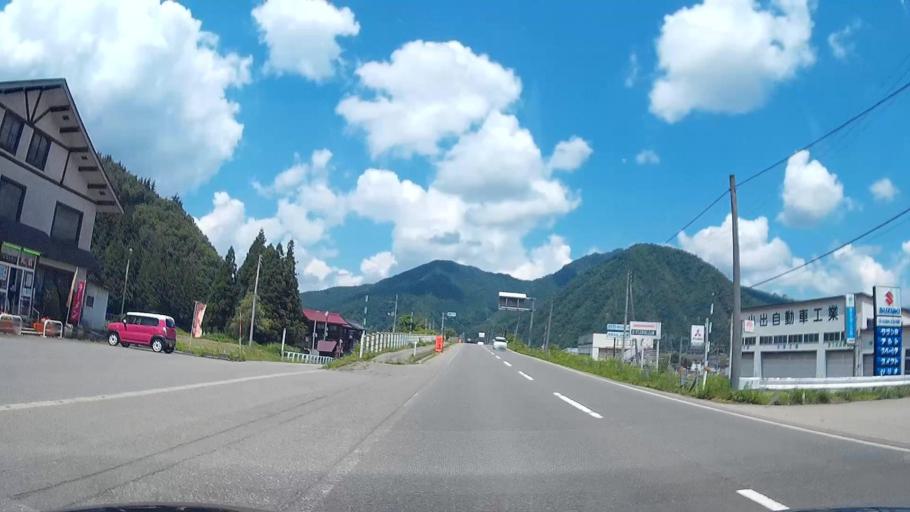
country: JP
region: Niigata
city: Shiozawa
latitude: 36.9259
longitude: 138.8240
